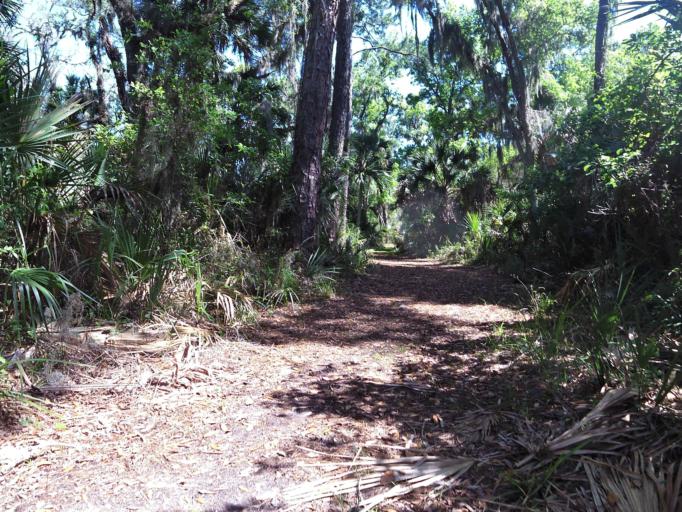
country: US
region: Florida
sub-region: Duval County
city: Atlantic Beach
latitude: 30.4417
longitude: -81.4775
